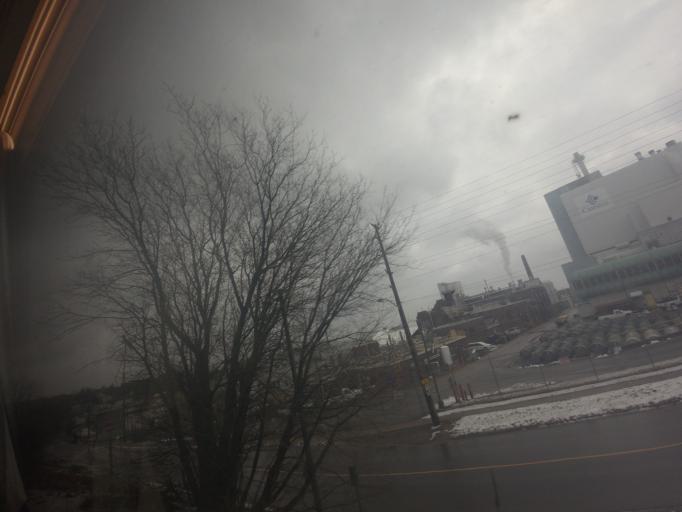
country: CA
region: Ontario
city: Cobourg
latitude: 43.9452
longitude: -78.2967
